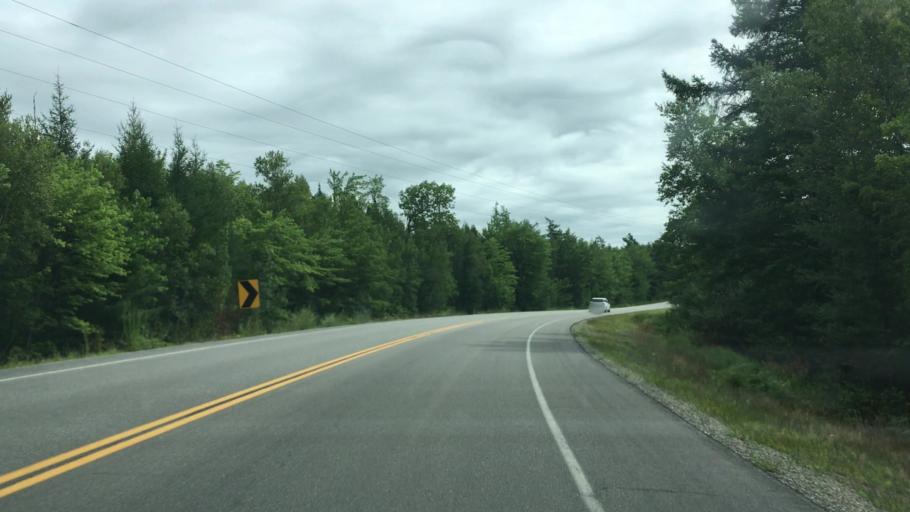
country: US
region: Maine
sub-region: Washington County
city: Machias
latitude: 45.0011
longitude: -67.5810
